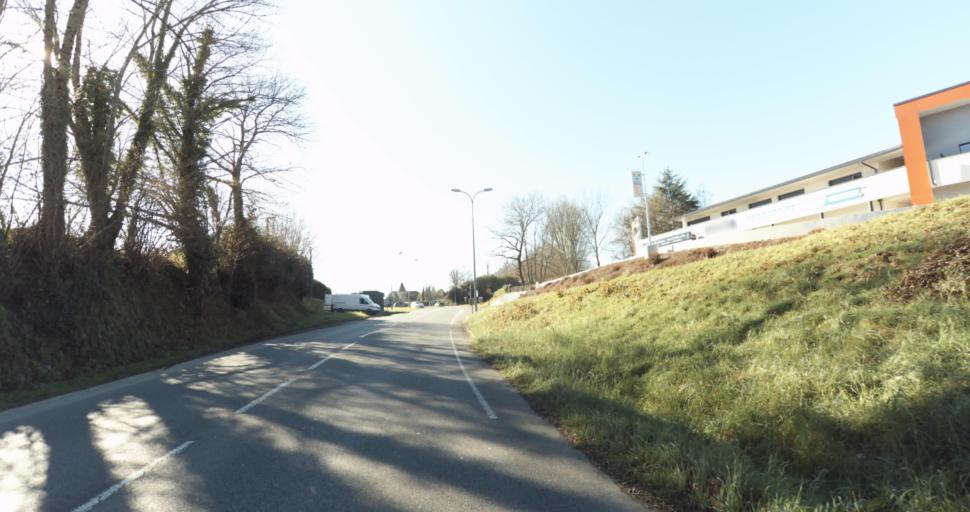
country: FR
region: Aquitaine
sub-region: Departement des Pyrenees-Atlantiques
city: Morlaas
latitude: 43.3517
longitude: -0.2559
